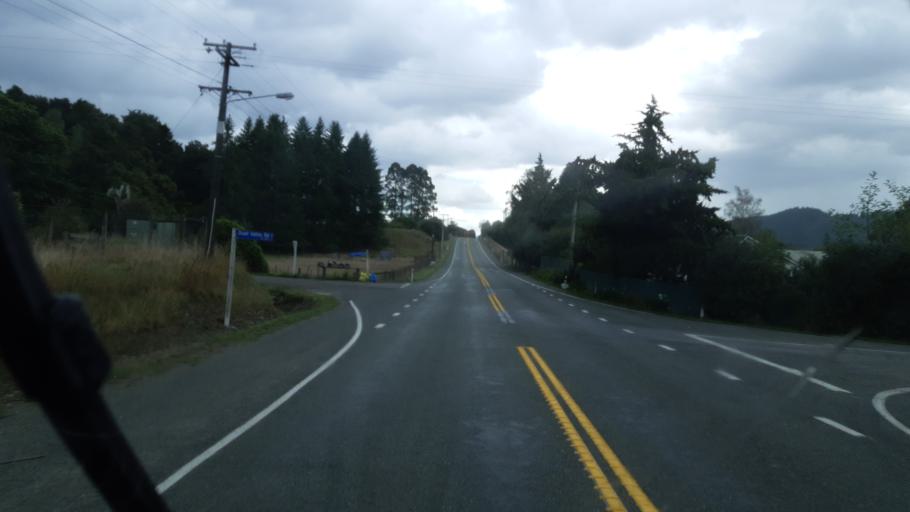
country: NZ
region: Tasman
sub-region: Tasman District
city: Wakefield
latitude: -41.4464
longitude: 172.9634
